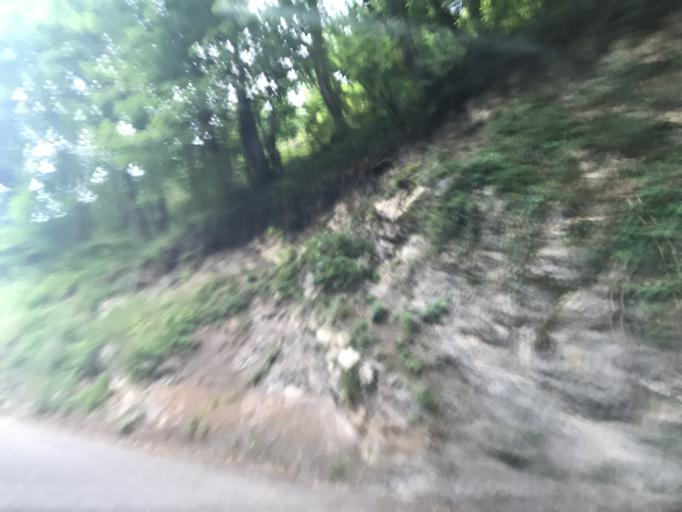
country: FR
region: Rhone-Alpes
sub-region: Departement de l'Isere
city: Saint-Vincent-de-Mercuze
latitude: 45.3932
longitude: 5.9428
